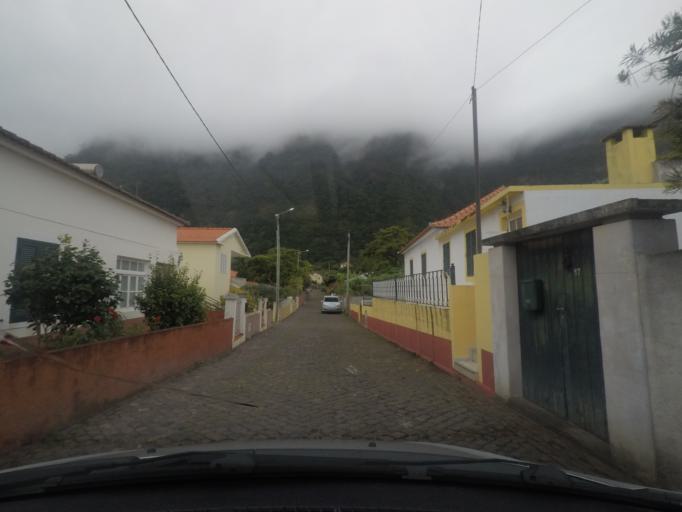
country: PT
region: Madeira
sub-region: Santana
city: Santana
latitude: 32.8284
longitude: -16.9543
